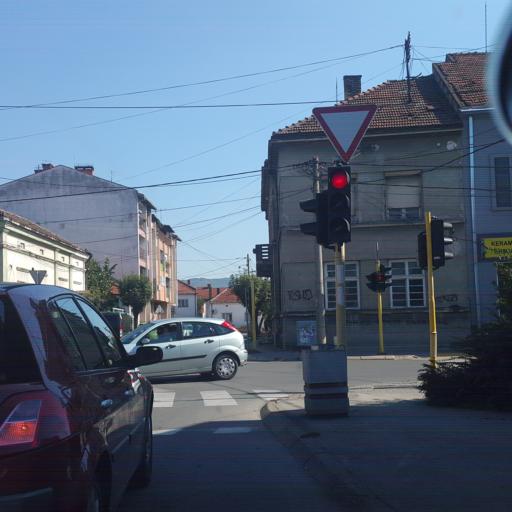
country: RS
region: Central Serbia
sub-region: Zajecarski Okrug
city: Knjazevac
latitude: 43.5686
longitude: 22.2592
